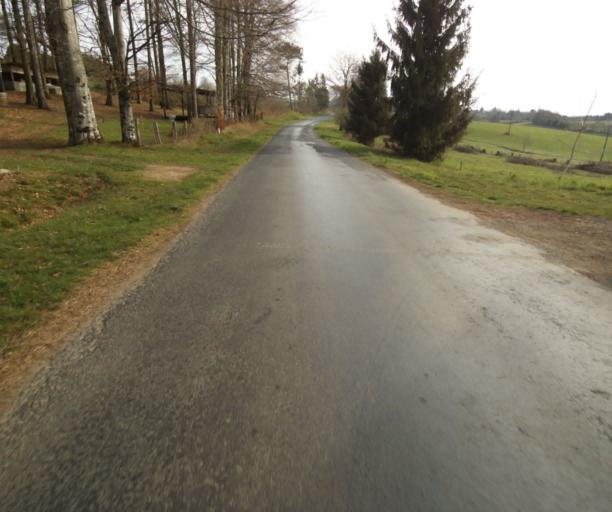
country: FR
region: Limousin
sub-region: Departement de la Correze
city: Chamboulive
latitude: 45.4330
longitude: 1.7678
